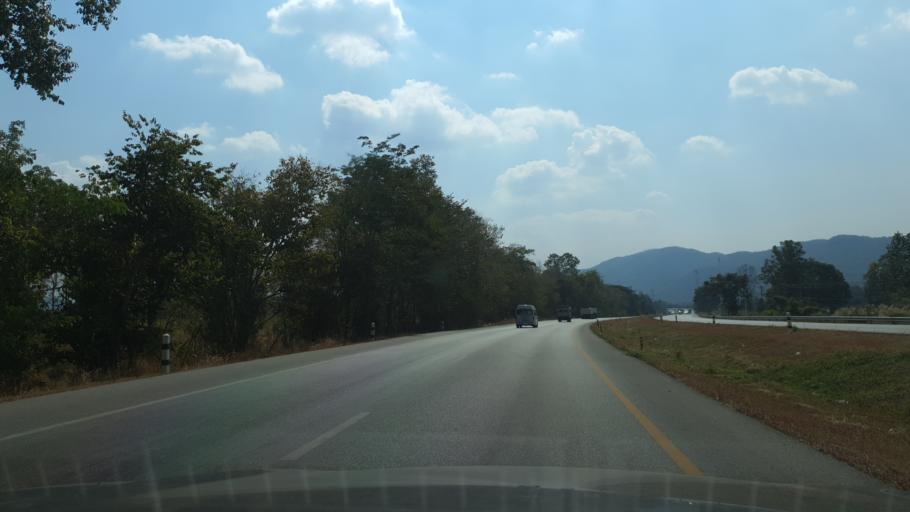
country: TH
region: Lampang
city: Mae Phrik
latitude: 17.3749
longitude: 99.1492
